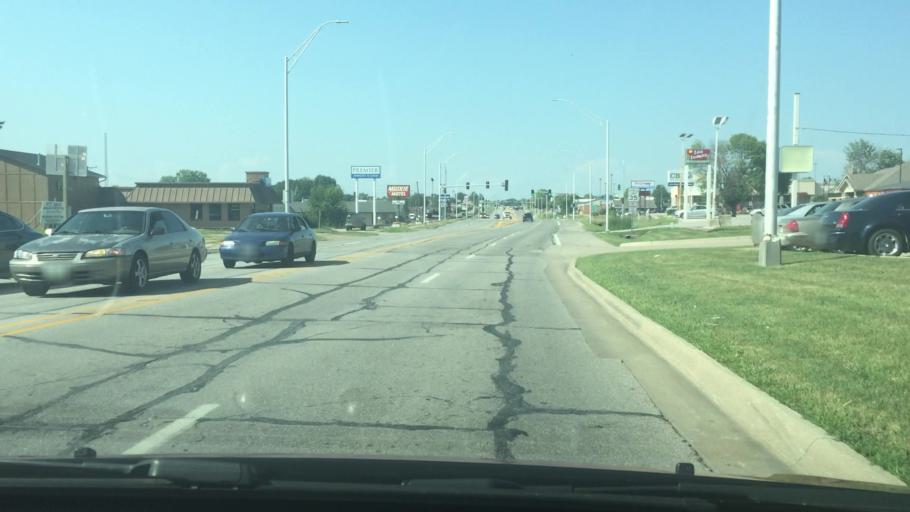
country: US
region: Iowa
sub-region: Muscatine County
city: Muscatine
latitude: 41.4424
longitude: -91.0305
